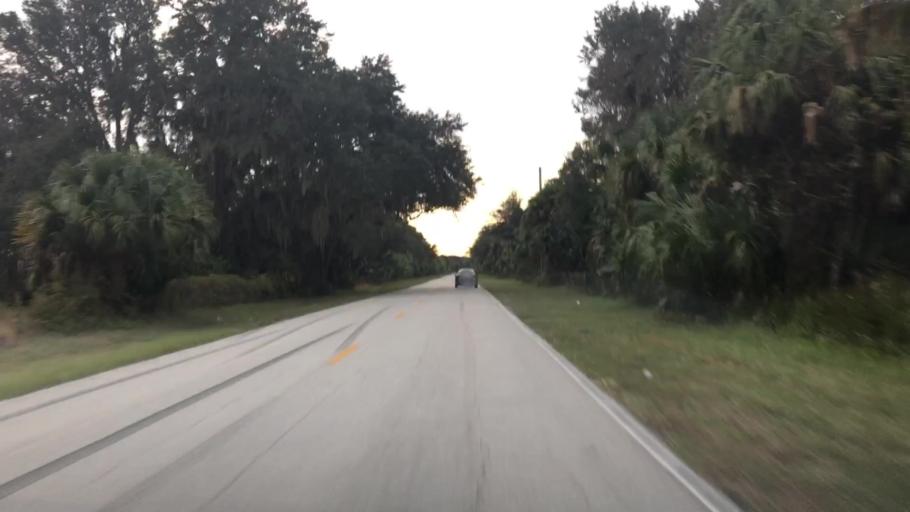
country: US
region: Florida
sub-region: Seminole County
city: Midway
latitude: 28.8251
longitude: -81.1876
